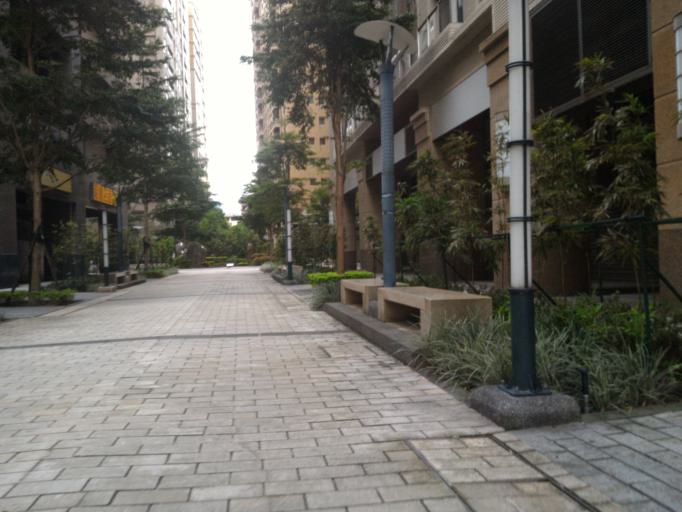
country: TW
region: Taiwan
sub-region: Taoyuan
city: Taoyuan
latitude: 24.9471
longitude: 121.3787
